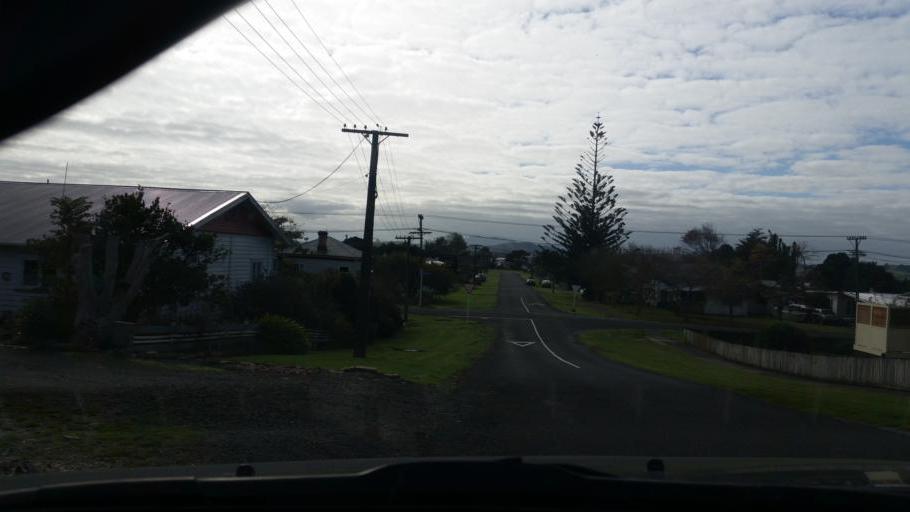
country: NZ
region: Northland
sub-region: Kaipara District
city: Dargaville
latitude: -35.9336
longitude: 173.8797
